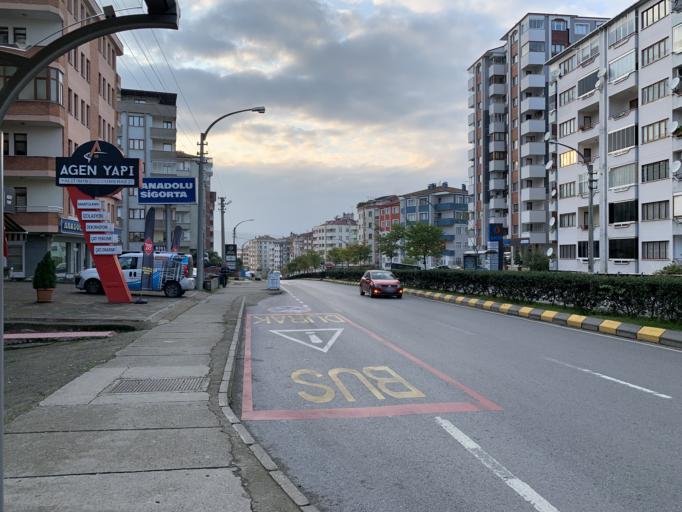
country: TR
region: Trabzon
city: Trabzon
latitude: 40.9967
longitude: 39.6818
